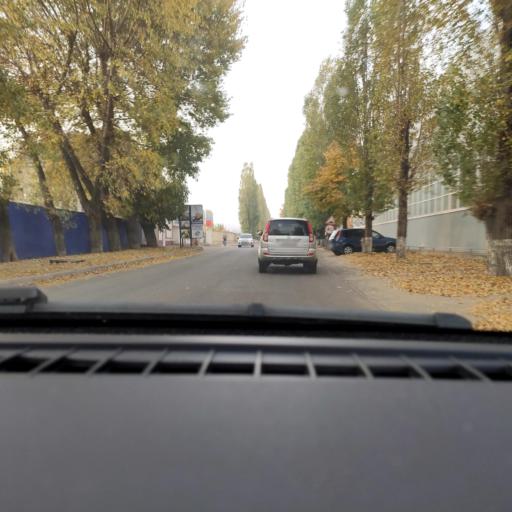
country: RU
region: Voronezj
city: Voronezh
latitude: 51.6518
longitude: 39.2808
